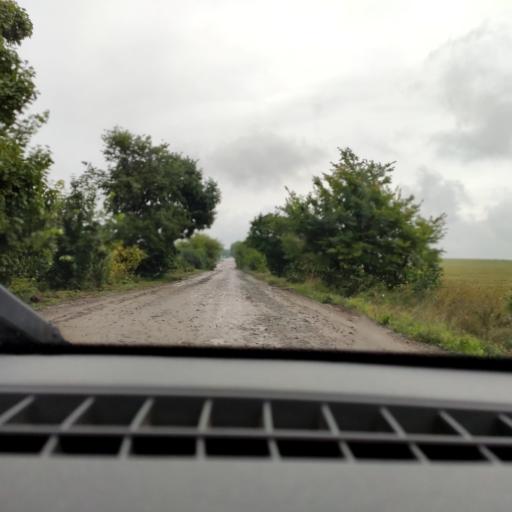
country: RU
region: Bashkortostan
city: Avdon
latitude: 54.7184
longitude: 55.7684
